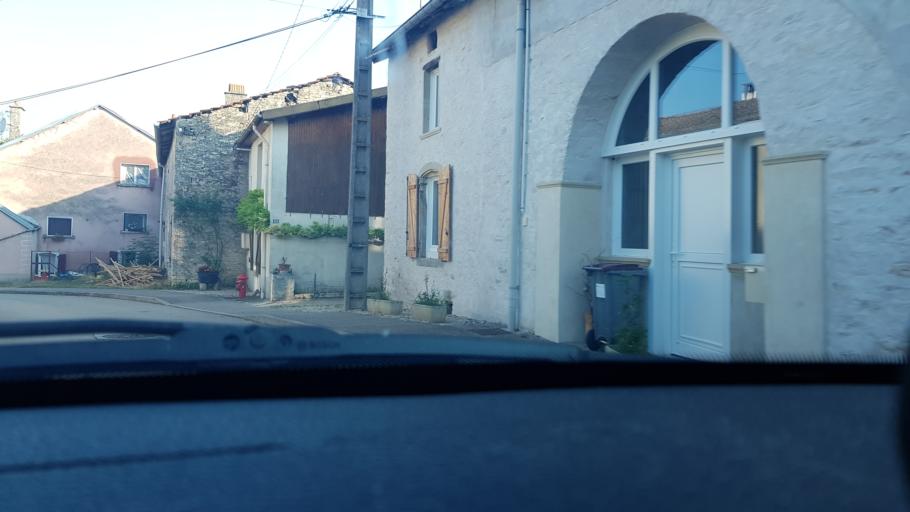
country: FR
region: Lorraine
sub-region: Departement des Vosges
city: Mirecourt
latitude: 48.3496
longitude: 6.1609
